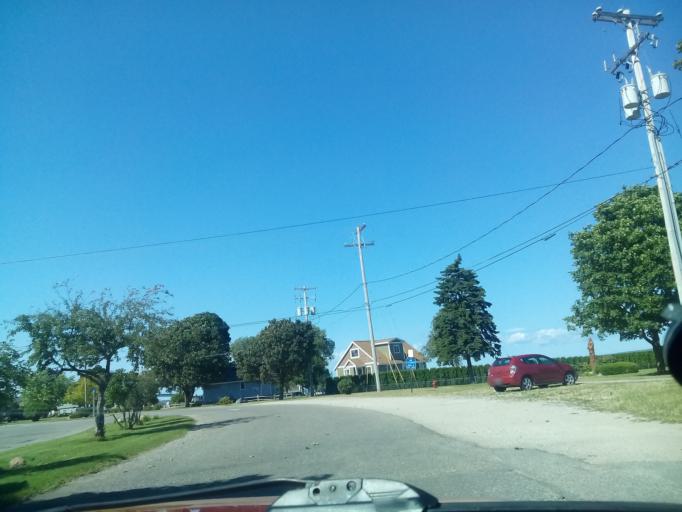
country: US
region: Michigan
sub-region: Mackinac County
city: Saint Ignace
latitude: 45.7832
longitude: -84.7241
